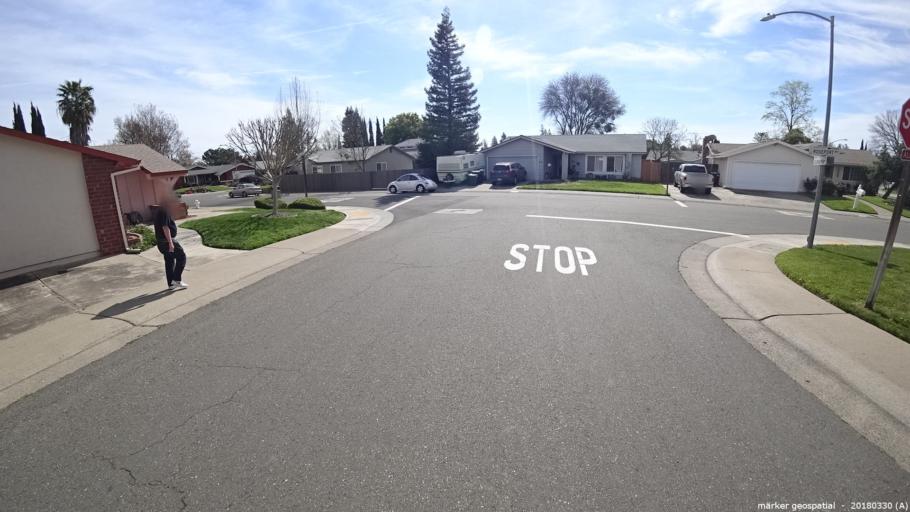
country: US
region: California
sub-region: Sacramento County
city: Rosemont
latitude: 38.5436
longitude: -121.3467
